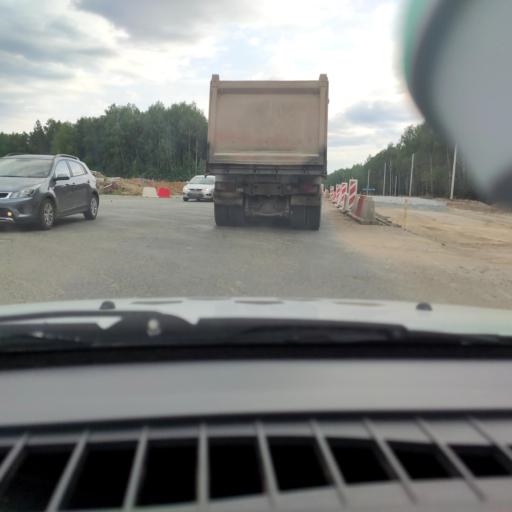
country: RU
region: Perm
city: Solikamsk
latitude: 59.5472
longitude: 56.7906
